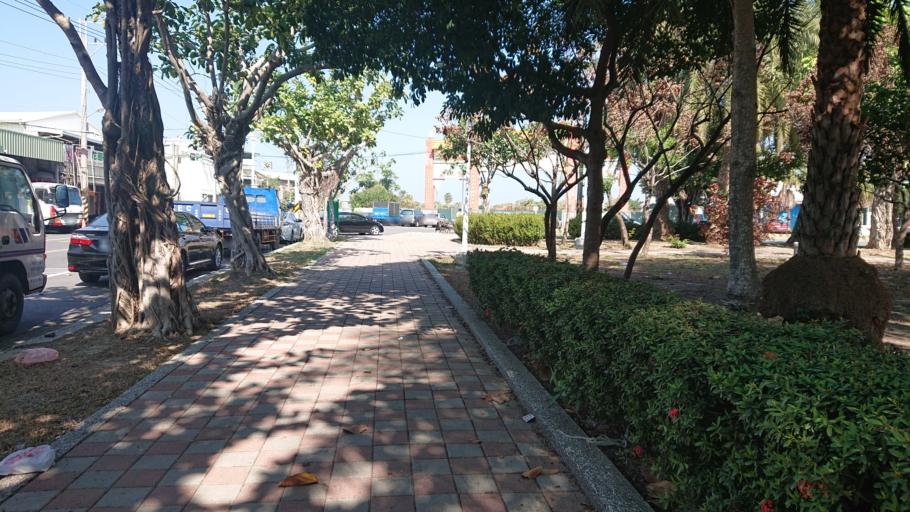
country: TW
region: Taiwan
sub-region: Tainan
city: Tainan
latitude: 23.0660
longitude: 120.1265
